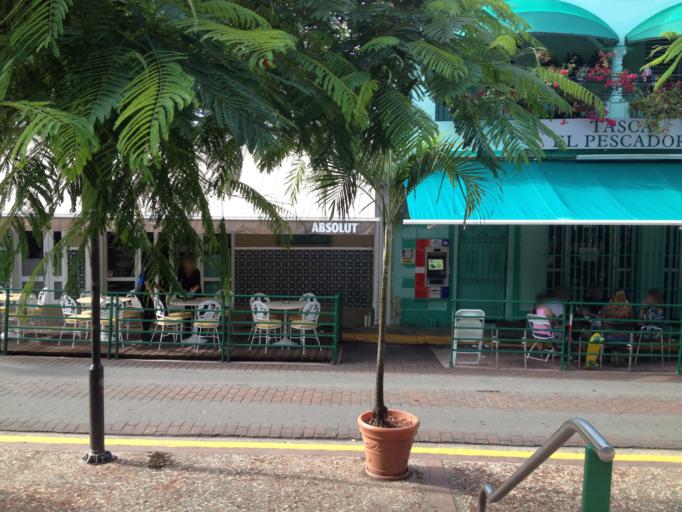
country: PR
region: San Juan
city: San Juan
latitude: 18.4505
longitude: -66.0706
